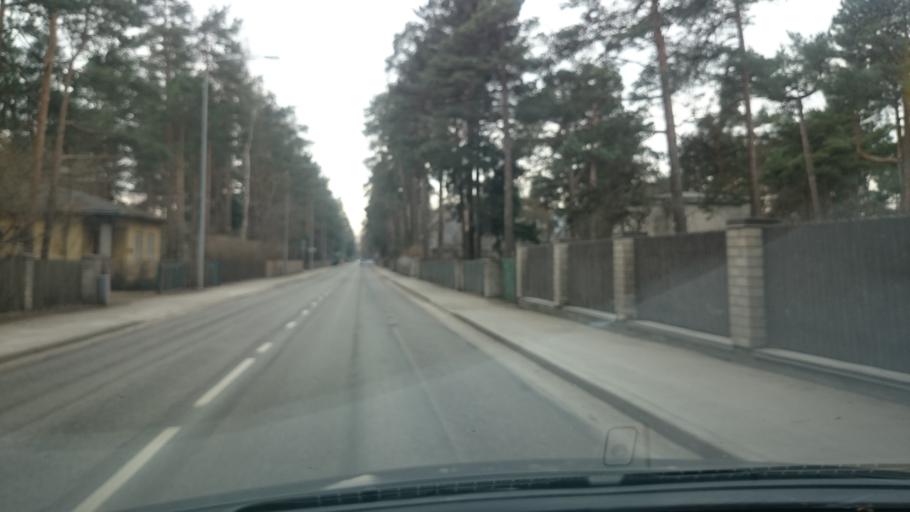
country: EE
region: Harju
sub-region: Saue vald
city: Laagri
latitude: 59.3773
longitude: 24.6354
